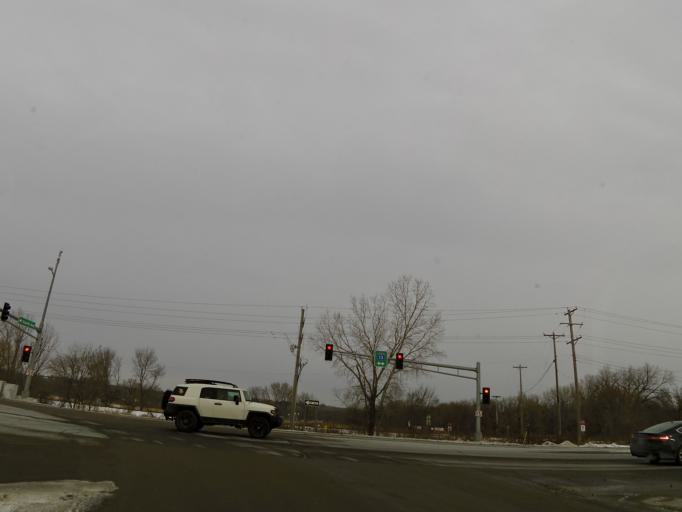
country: US
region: Minnesota
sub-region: Scott County
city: Savage
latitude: 44.7789
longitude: -93.3444
